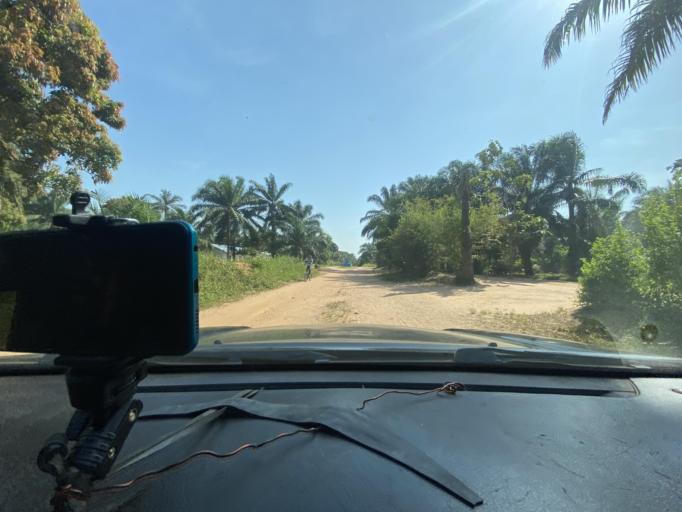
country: CD
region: Kasai-Oriental
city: Kabinda
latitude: -6.1245
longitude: 24.5269
